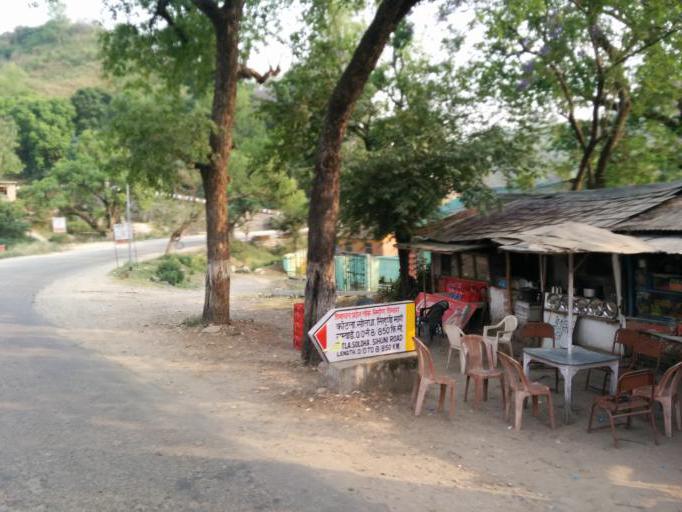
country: IN
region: Himachal Pradesh
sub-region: Kangra
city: Kotla
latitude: 32.2371
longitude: 76.0478
